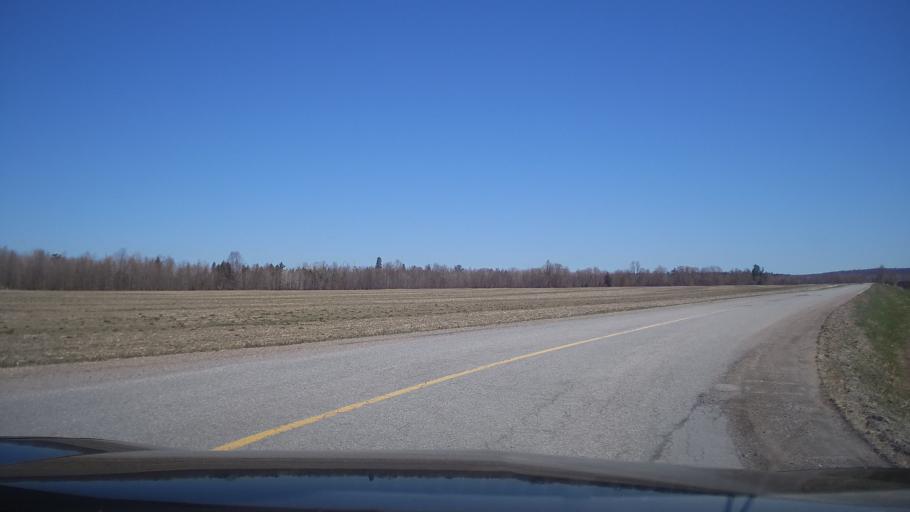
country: CA
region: Quebec
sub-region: Outaouais
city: Shawville
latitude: 45.5378
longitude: -76.3942
